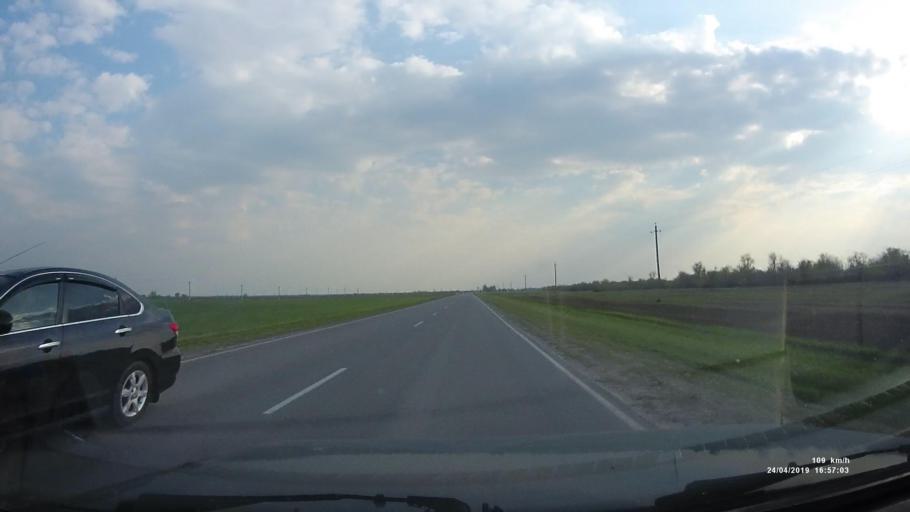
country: RU
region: Rostov
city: Proletarsk
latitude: 46.6425
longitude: 41.6721
